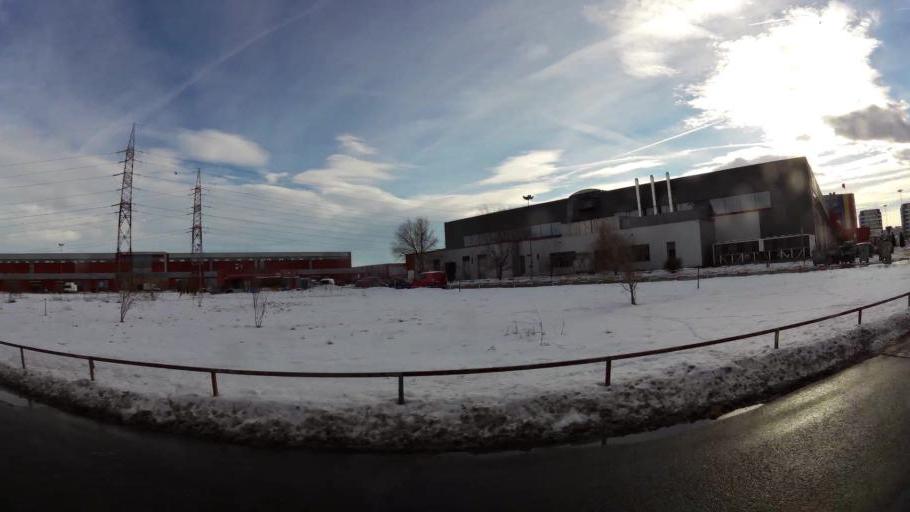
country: RO
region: Ilfov
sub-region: Voluntari City
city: Voluntari
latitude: 44.4787
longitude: 26.1827
